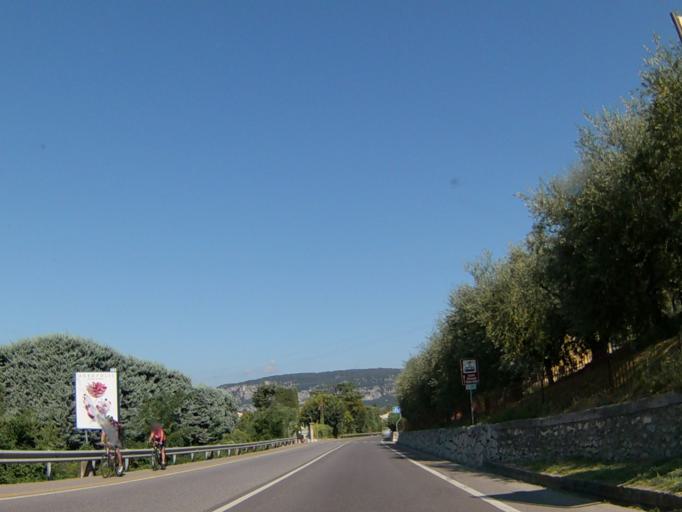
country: IT
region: Veneto
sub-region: Provincia di Verona
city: Garda
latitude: 45.5604
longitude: 10.7165
